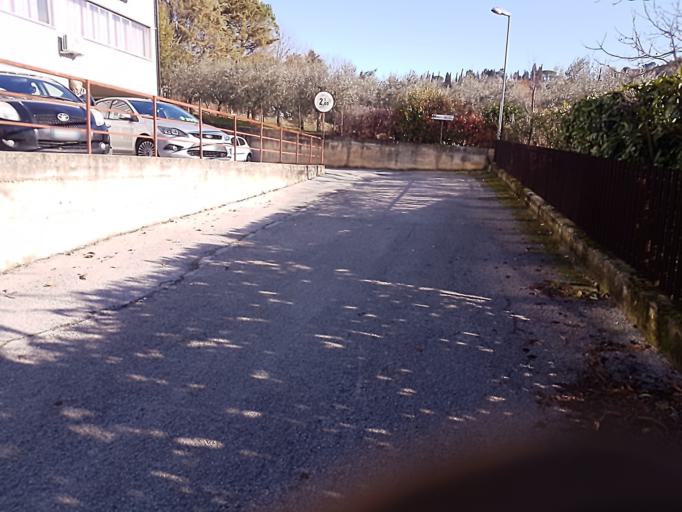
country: IT
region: Umbria
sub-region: Provincia di Perugia
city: Perugia
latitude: 43.0929
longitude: 12.3707
